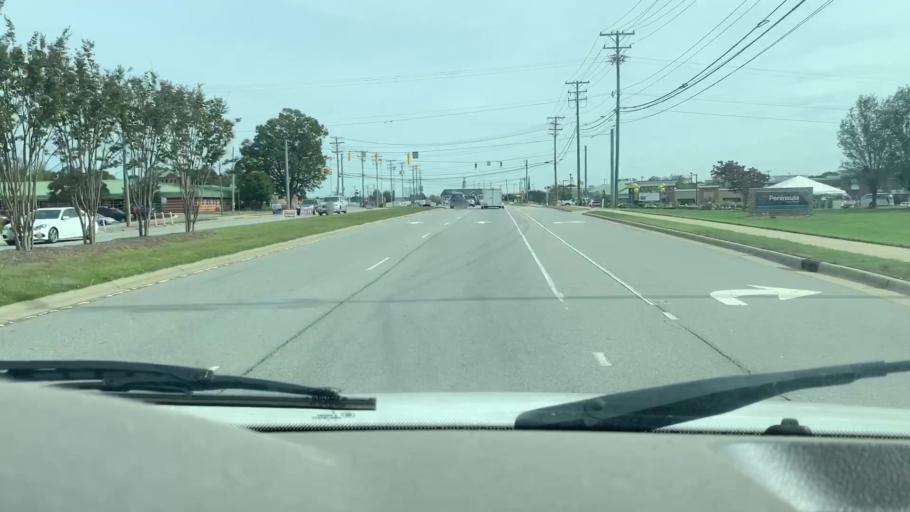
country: US
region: North Carolina
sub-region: Iredell County
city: Mooresville
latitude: 35.5814
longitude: -80.8792
